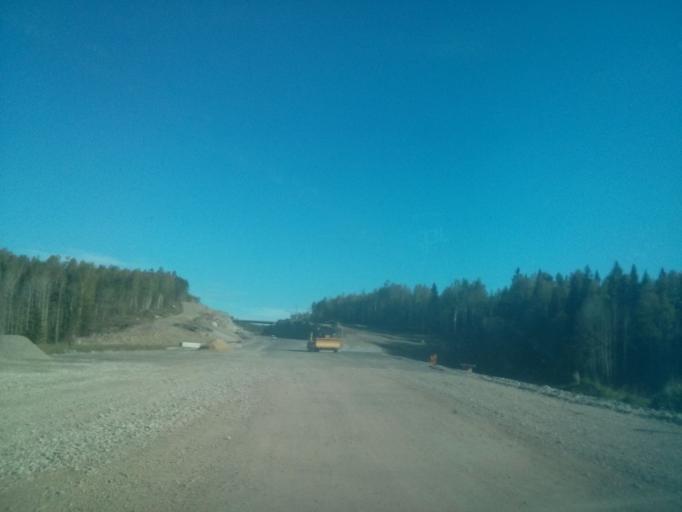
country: SE
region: Vaesternorrland
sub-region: Sundsvalls Kommun
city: Nolby
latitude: 62.2960
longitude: 17.3494
